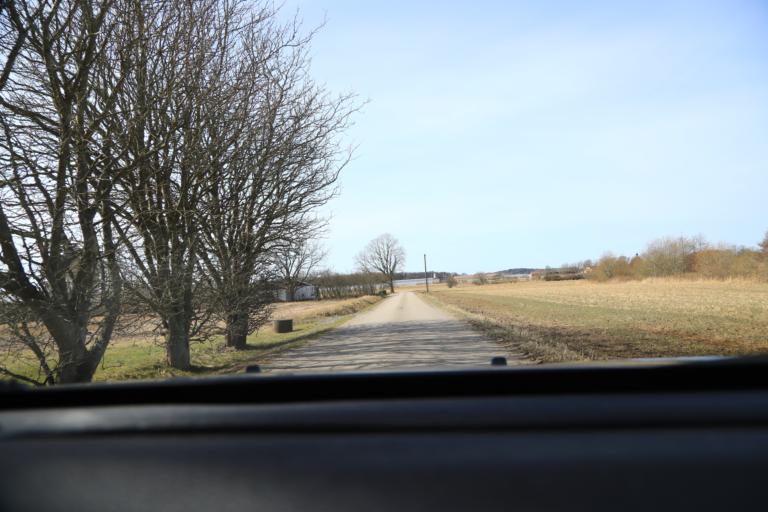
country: SE
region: Halland
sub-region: Kungsbacka Kommun
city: Frillesas
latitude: 57.2592
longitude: 12.2106
